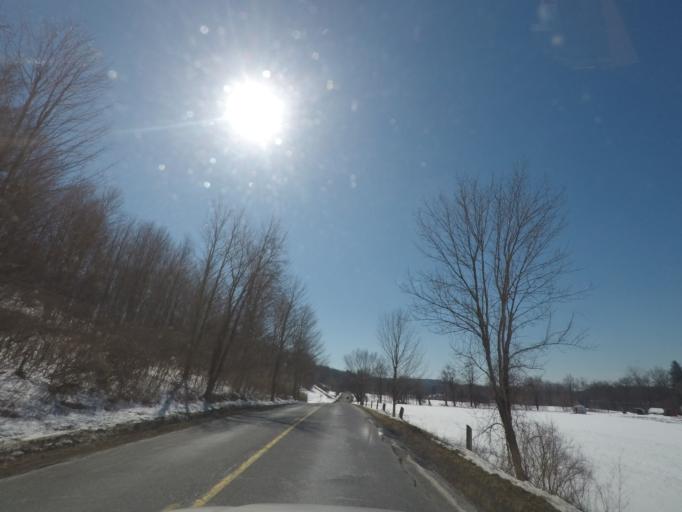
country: US
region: New York
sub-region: Saratoga County
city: Stillwater
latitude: 42.9489
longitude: -73.6251
